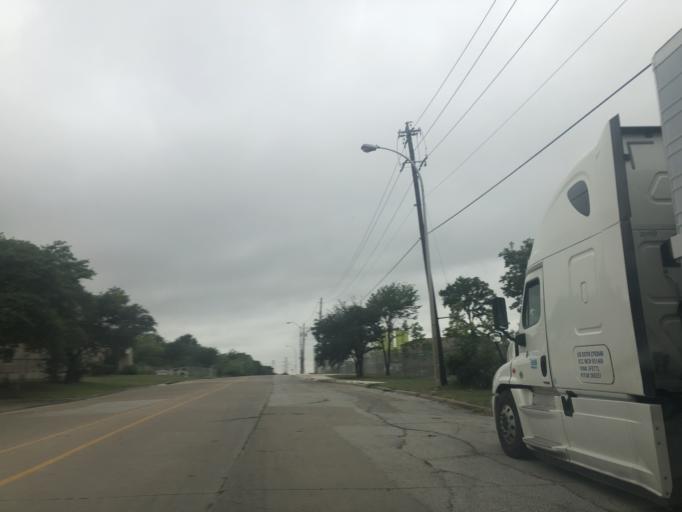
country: US
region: Texas
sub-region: Dallas County
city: Cockrell Hill
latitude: 32.7751
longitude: -96.8661
